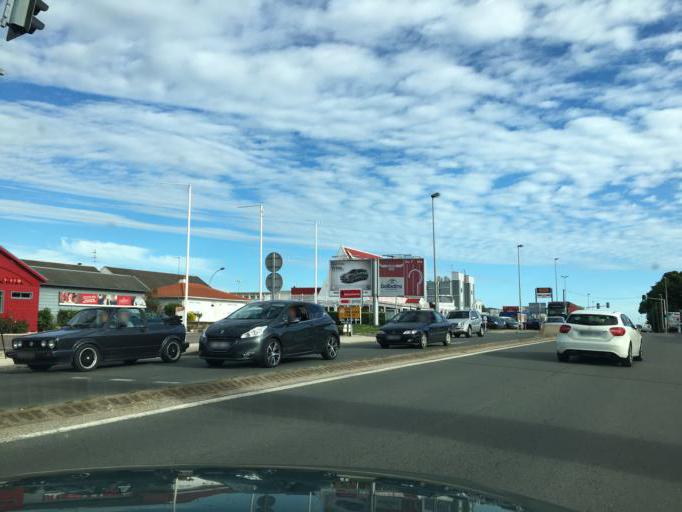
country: FR
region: Centre
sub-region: Departement du Loiret
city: Saran
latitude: 47.9446
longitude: 1.8923
